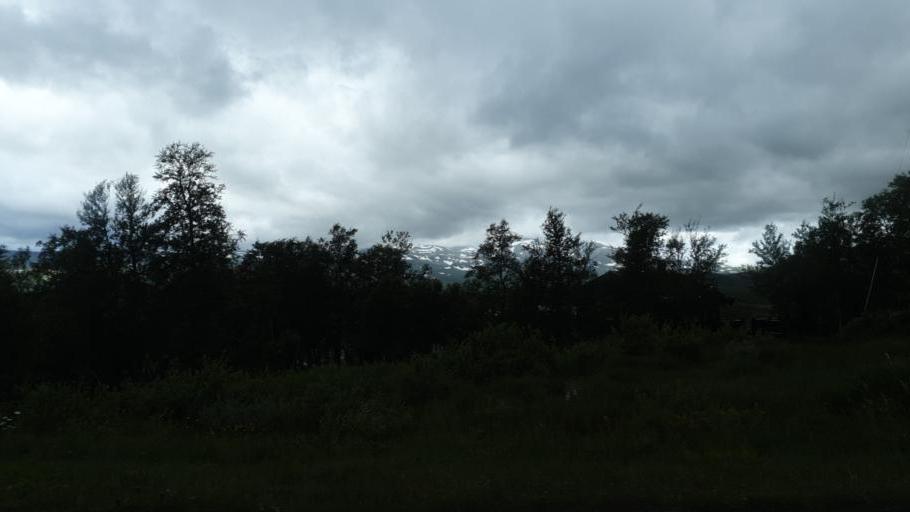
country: NO
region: Oppland
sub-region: Vestre Slidre
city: Slidre
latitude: 61.2599
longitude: 8.8745
